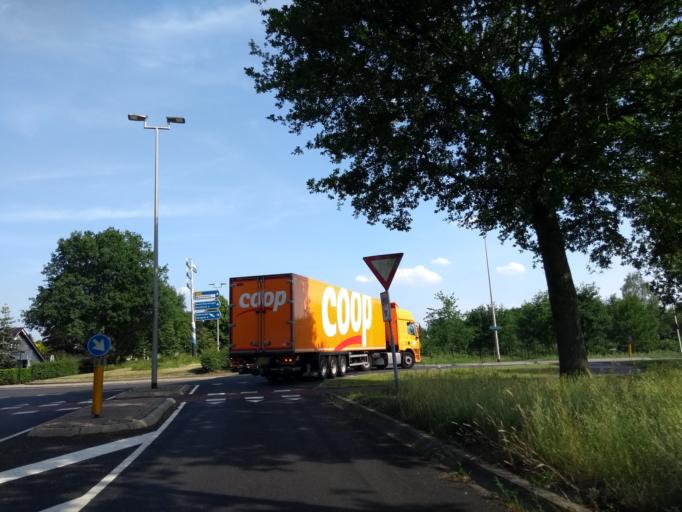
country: DE
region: Lower Saxony
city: Nordhorn
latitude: 52.3783
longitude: 6.9957
